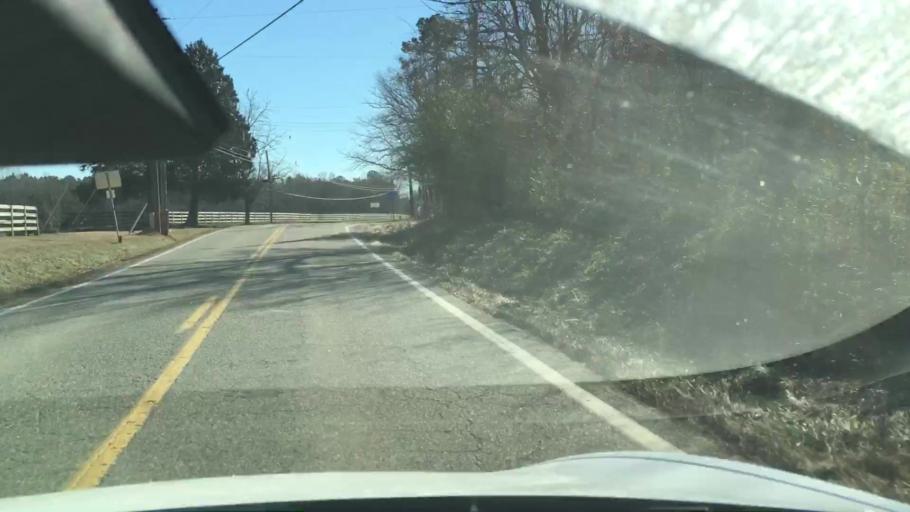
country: US
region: Virginia
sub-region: Henrico County
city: Short Pump
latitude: 37.5686
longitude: -77.7120
